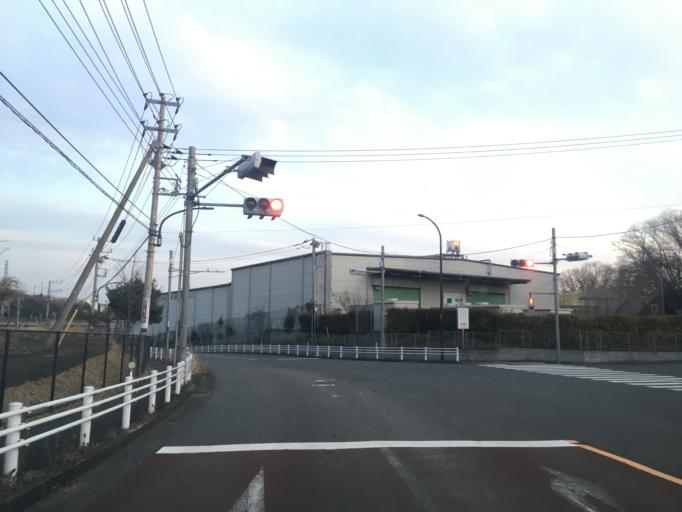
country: JP
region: Tokyo
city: Hino
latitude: 35.6019
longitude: 139.3878
